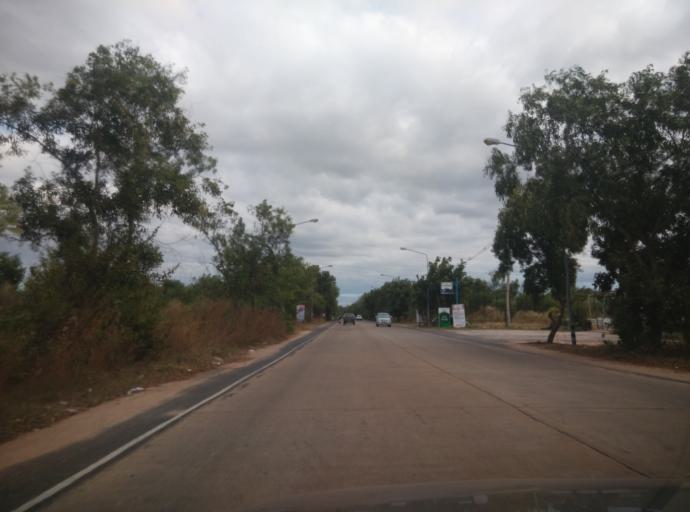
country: TH
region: Sisaket
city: Si Sa Ket
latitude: 15.1220
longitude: 104.3480
